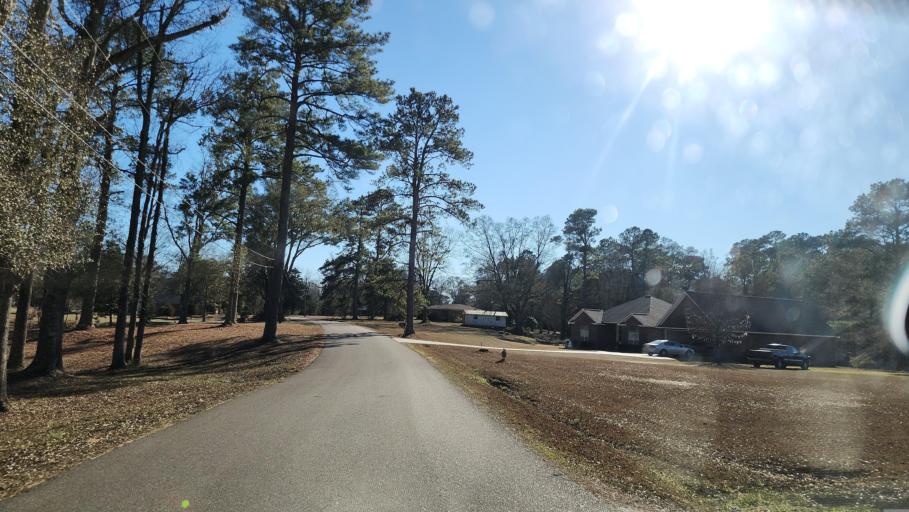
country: US
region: Mississippi
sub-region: Jones County
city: Laurel
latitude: 31.7080
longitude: -89.0929
